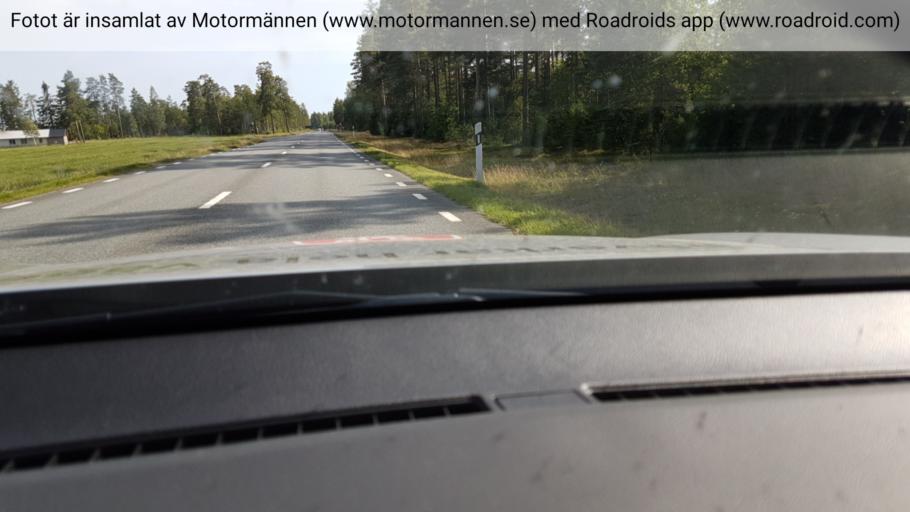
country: SE
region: Joenkoeping
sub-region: Eksjo Kommun
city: Eksjoe
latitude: 57.6150
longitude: 14.9703
